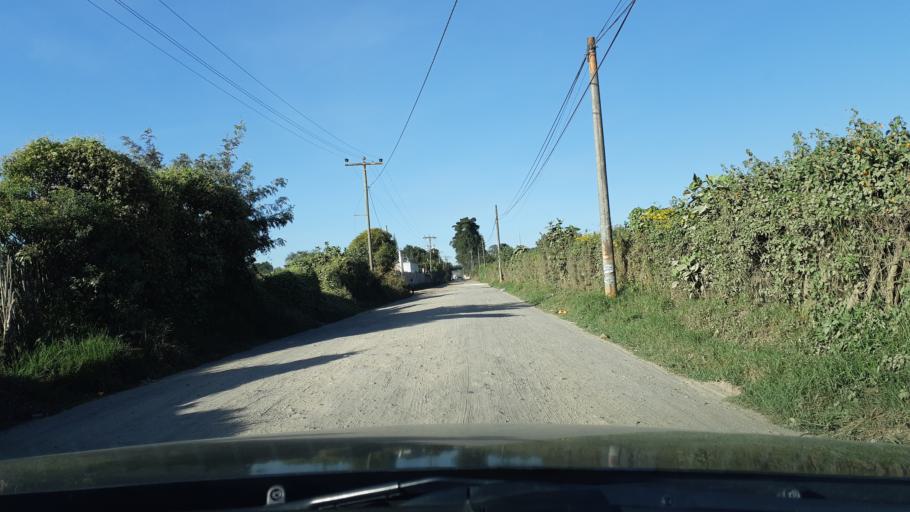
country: GT
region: Chimaltenango
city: El Tejar
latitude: 14.6368
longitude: -90.7999
